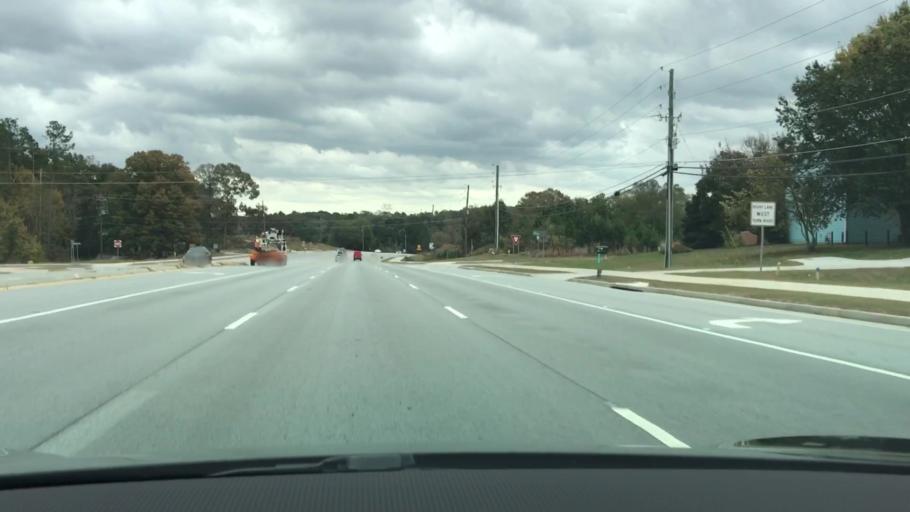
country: US
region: Georgia
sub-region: Hall County
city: Flowery Branch
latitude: 34.1145
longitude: -83.8993
